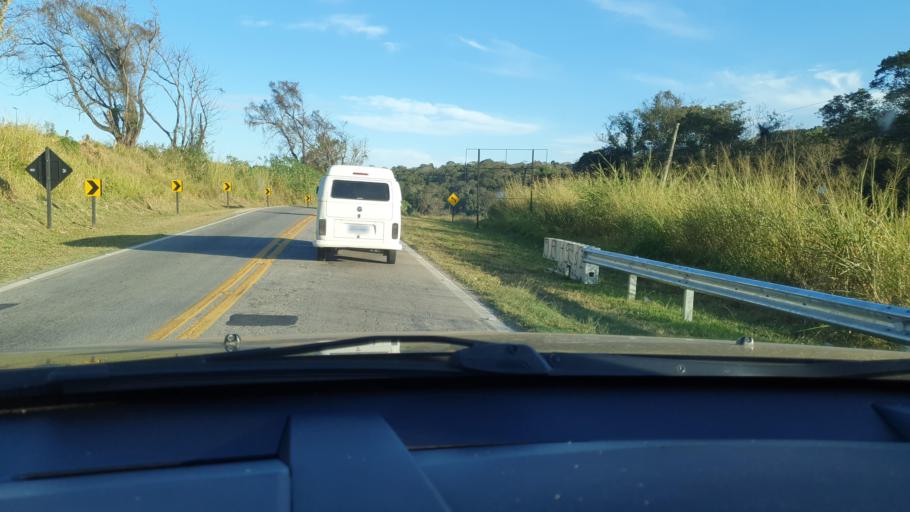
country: BR
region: Sao Paulo
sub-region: Piedade
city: Piedade
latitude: -23.7128
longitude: -47.3950
